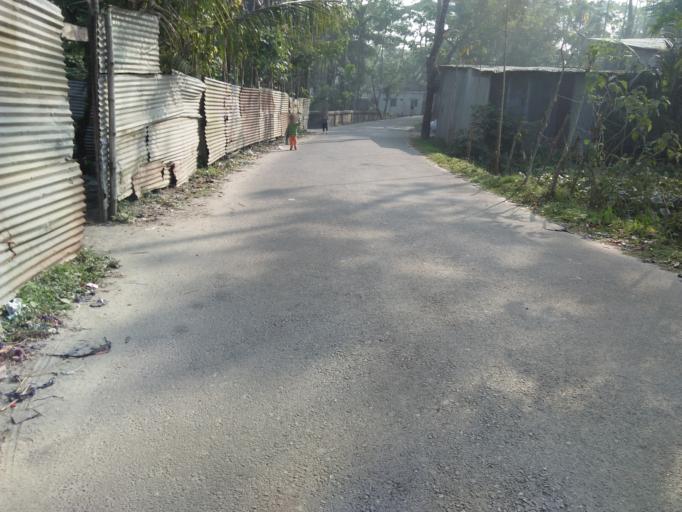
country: BD
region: Barisal
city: Bhola
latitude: 22.6797
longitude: 90.6395
